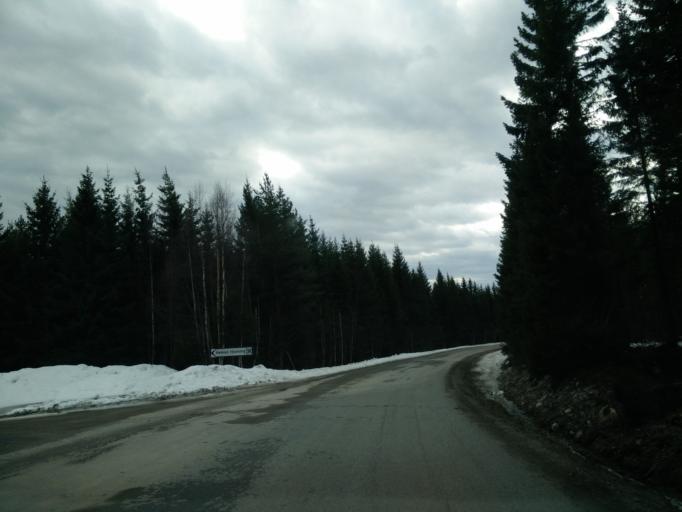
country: SE
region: Vaesternorrland
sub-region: Haernoesands Kommun
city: Haernoesand
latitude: 62.7110
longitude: 18.0420
